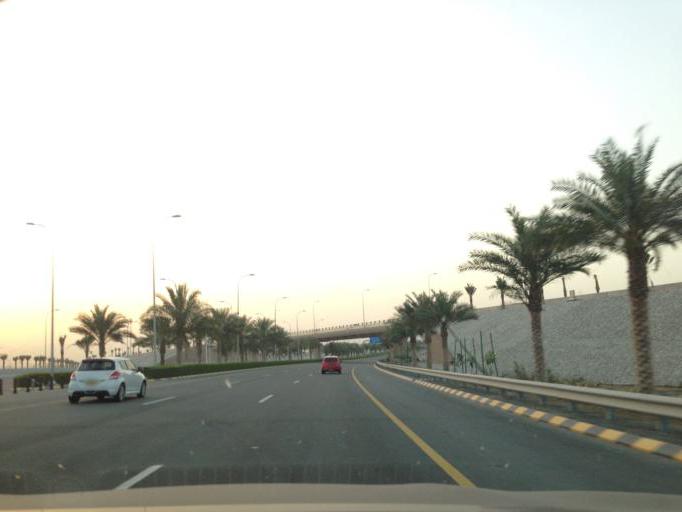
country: OM
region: Muhafazat Masqat
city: Bawshar
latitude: 23.5993
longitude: 58.3282
